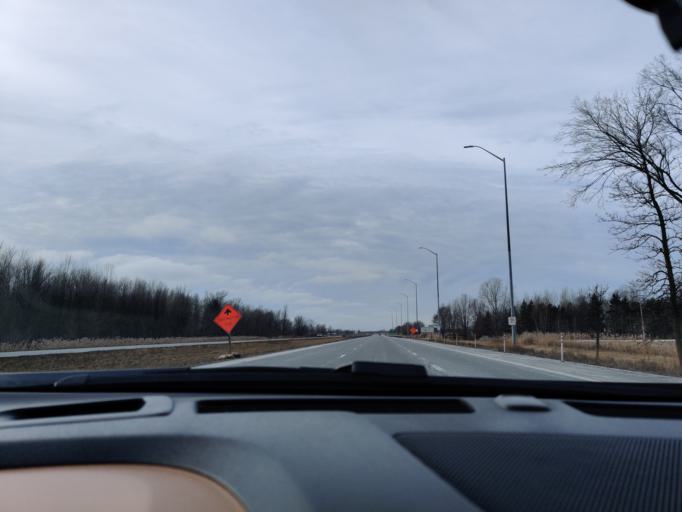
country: CA
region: Quebec
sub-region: Monteregie
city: Les Coteaux
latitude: 45.1999
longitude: -74.3661
